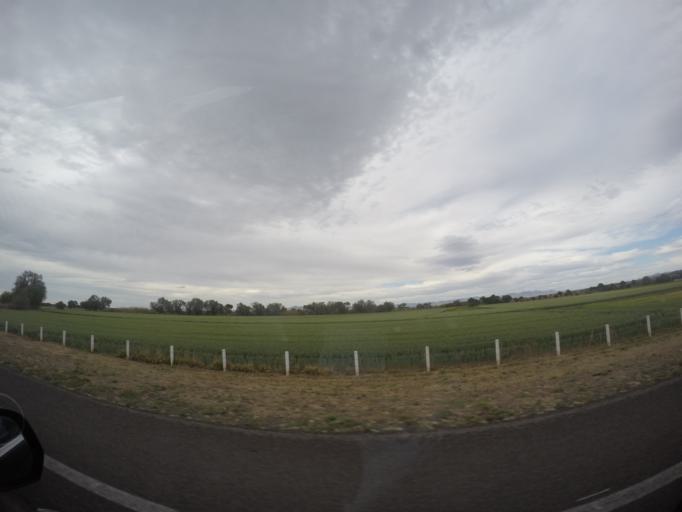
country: MX
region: Guanajuato
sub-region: Irapuato
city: Serrano
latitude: 20.7789
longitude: -101.4082
